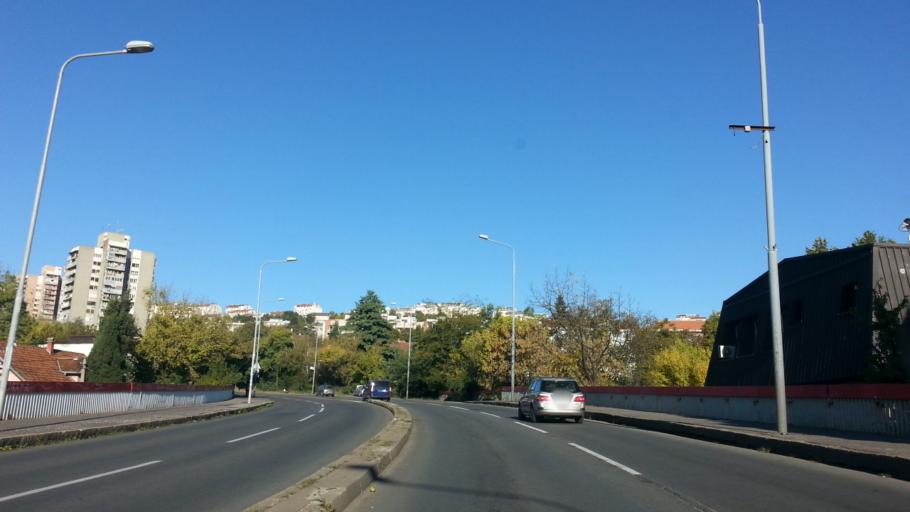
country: RS
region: Central Serbia
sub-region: Belgrade
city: Rakovica
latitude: 44.7450
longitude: 20.4414
